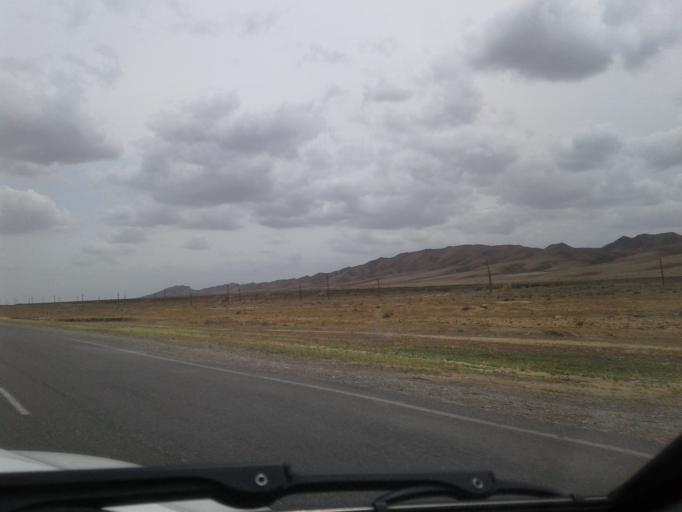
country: IR
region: Razavi Khorasan
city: Dargaz
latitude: 37.6157
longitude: 59.1844
